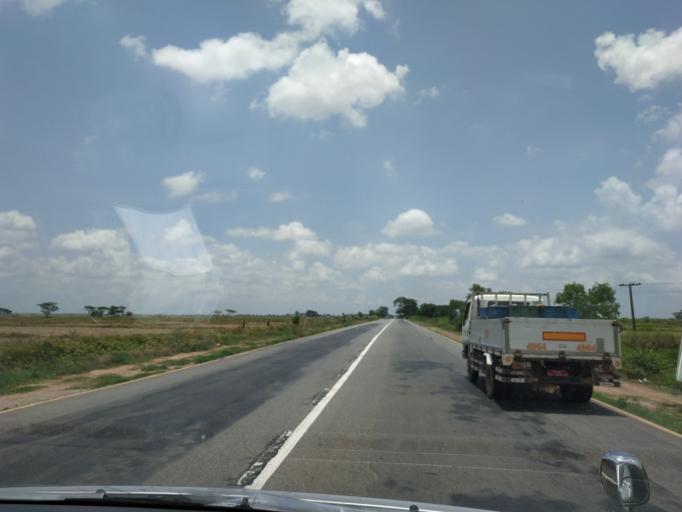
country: MM
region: Bago
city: Bago
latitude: 17.4628
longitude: 96.5928
